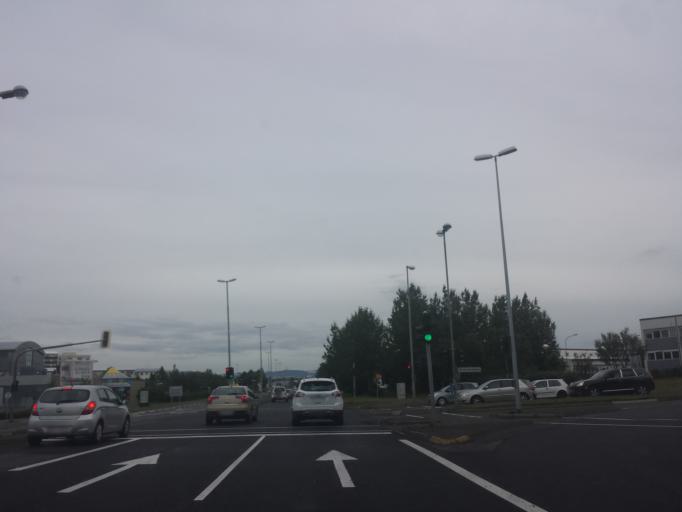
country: IS
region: Capital Region
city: Reykjavik
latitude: 64.1345
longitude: -21.8712
